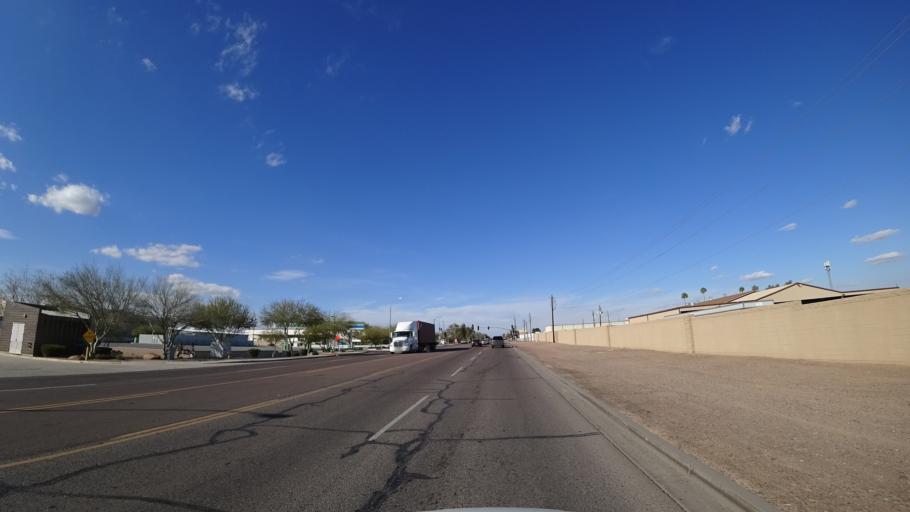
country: US
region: Arizona
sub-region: Maricopa County
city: Tolleson
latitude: 33.4395
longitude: -112.2382
